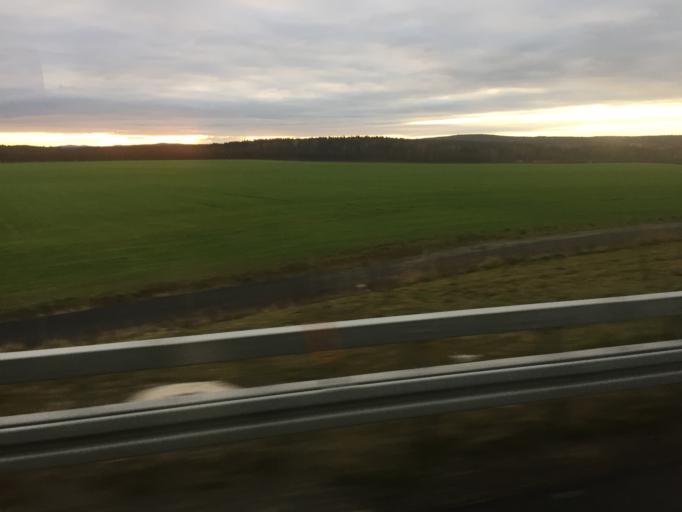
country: DE
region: Brandenburg
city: Grosskmehlen
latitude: 51.3586
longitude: 13.7315
